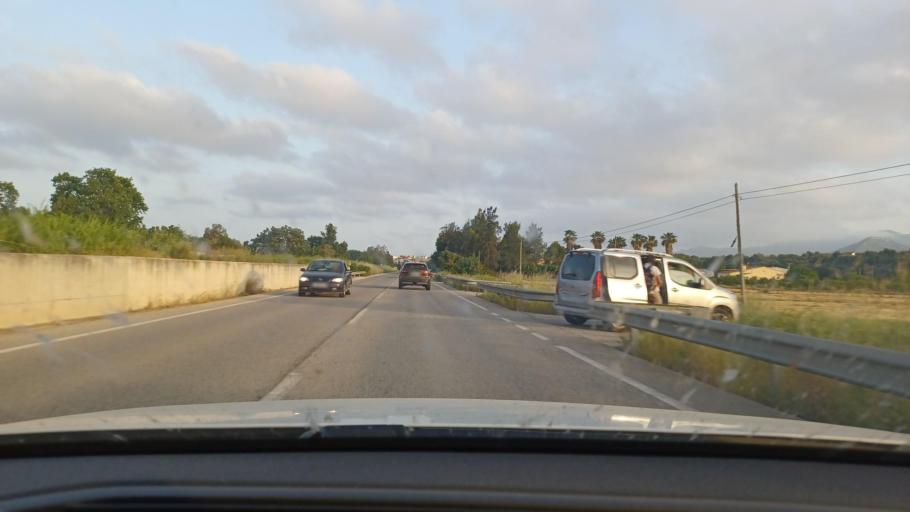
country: ES
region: Catalonia
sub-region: Provincia de Tarragona
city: Amposta
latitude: 40.7246
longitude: 0.5724
